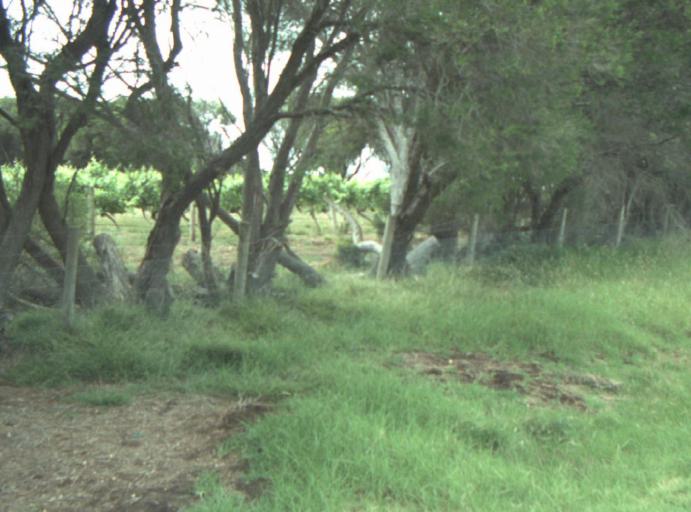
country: AU
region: Victoria
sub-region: Greater Geelong
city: Wandana Heights
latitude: -38.2089
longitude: 144.2840
